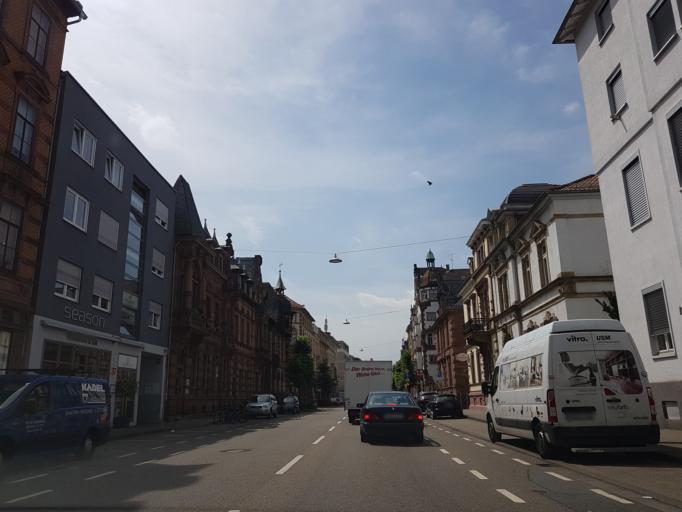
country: DE
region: Baden-Wuerttemberg
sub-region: Karlsruhe Region
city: Heidelberg
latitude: 49.4046
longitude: 8.6923
